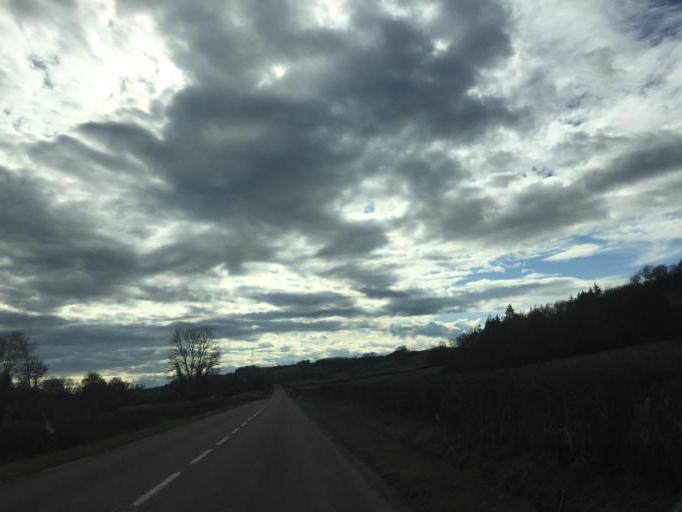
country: FR
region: Bourgogne
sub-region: Departement de l'Yonne
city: Avallon
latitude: 47.4794
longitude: 3.8405
